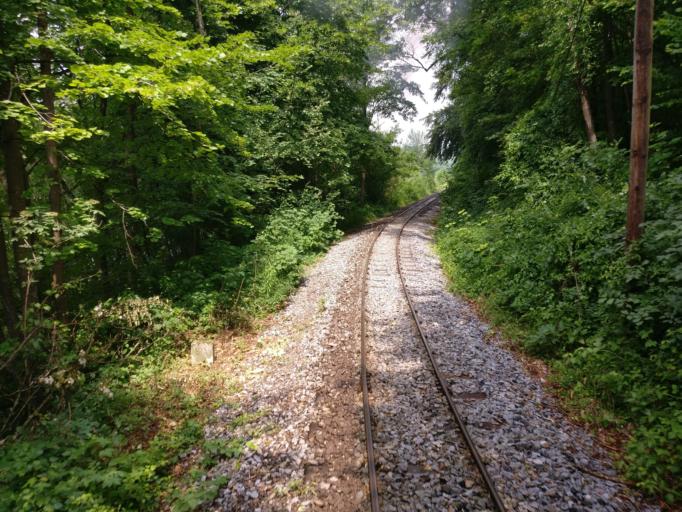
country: AT
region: Upper Austria
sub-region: Politischer Bezirk Steyr-Land
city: Sierning
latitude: 48.0382
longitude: 14.3347
